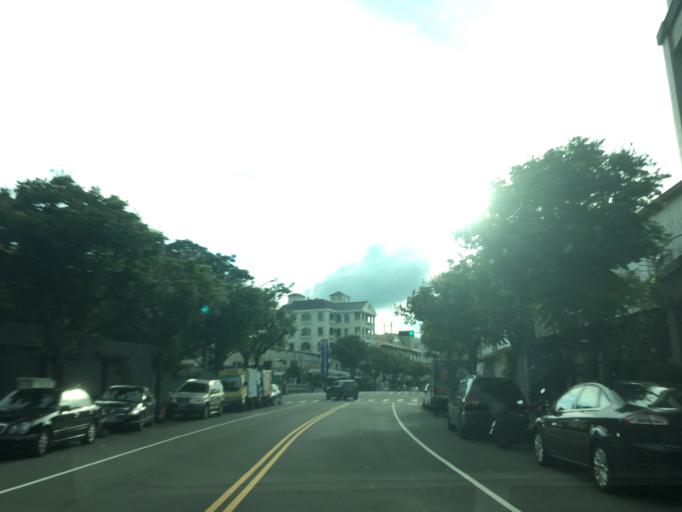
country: TW
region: Taiwan
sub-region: Taichung City
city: Taichung
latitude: 24.1320
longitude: 120.6387
